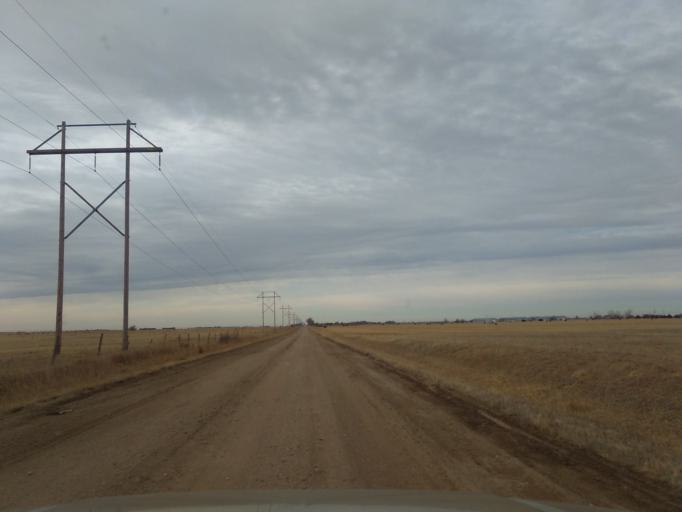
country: US
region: Nebraska
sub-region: Buffalo County
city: Shelton
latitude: 40.6548
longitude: -98.7346
